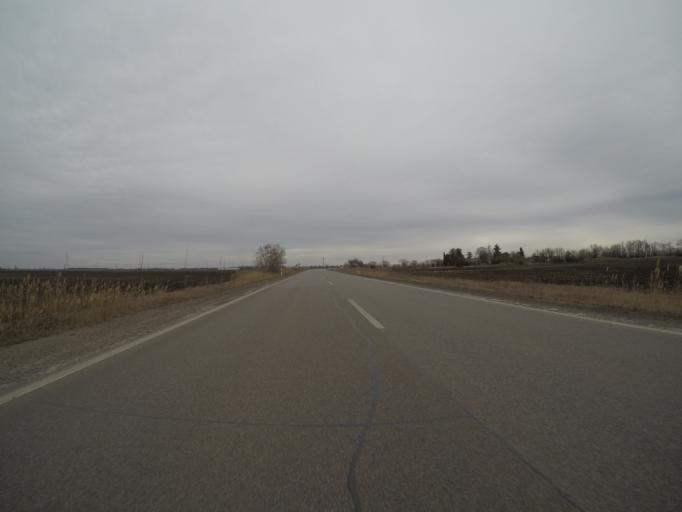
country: HU
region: Jasz-Nagykun-Szolnok
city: Jaszapati
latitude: 47.5085
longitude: 20.1041
